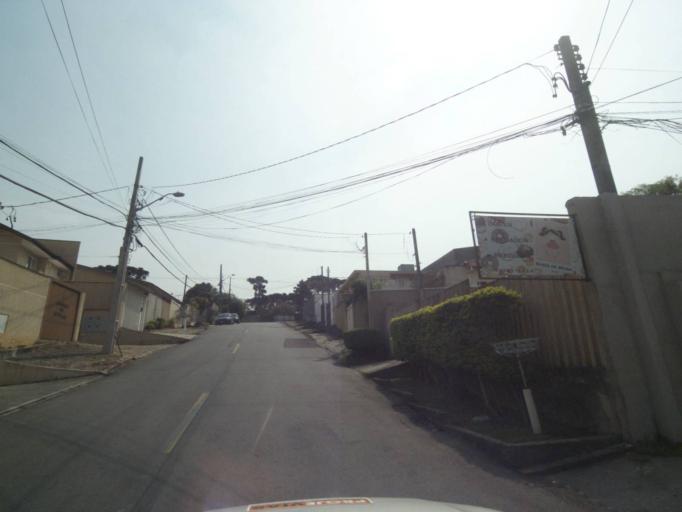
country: BR
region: Parana
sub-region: Pinhais
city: Pinhais
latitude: -25.4748
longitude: -49.2222
